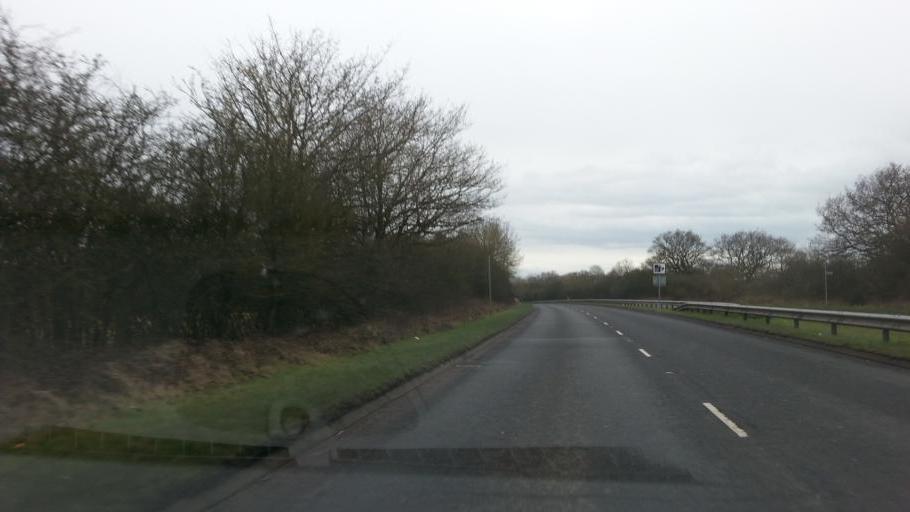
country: GB
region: England
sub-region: Solihull
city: Tidbury Green
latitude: 52.3980
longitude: -1.8940
